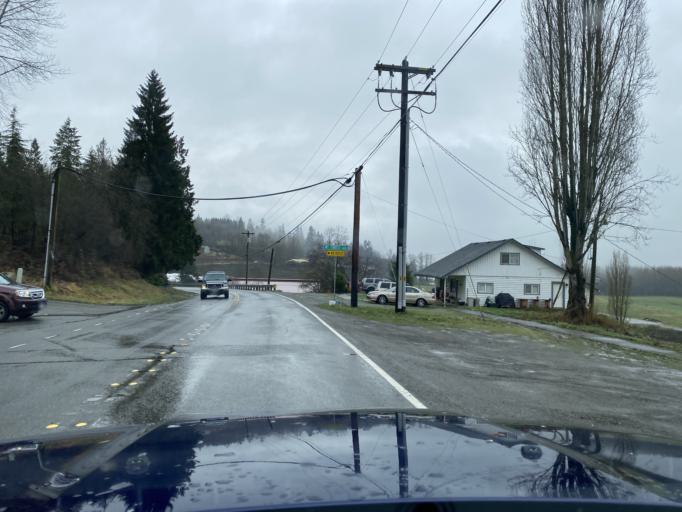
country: US
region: Washington
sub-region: King County
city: Duvall
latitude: 47.7859
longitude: -121.9986
